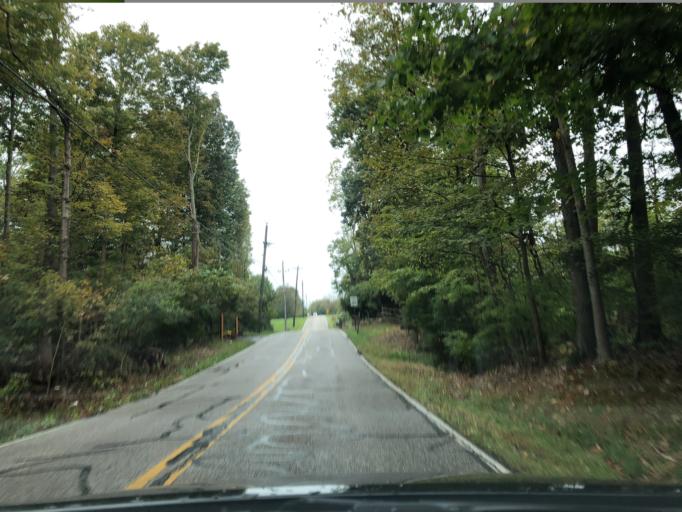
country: US
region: Ohio
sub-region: Hamilton County
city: Loveland
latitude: 39.2476
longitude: -84.2330
